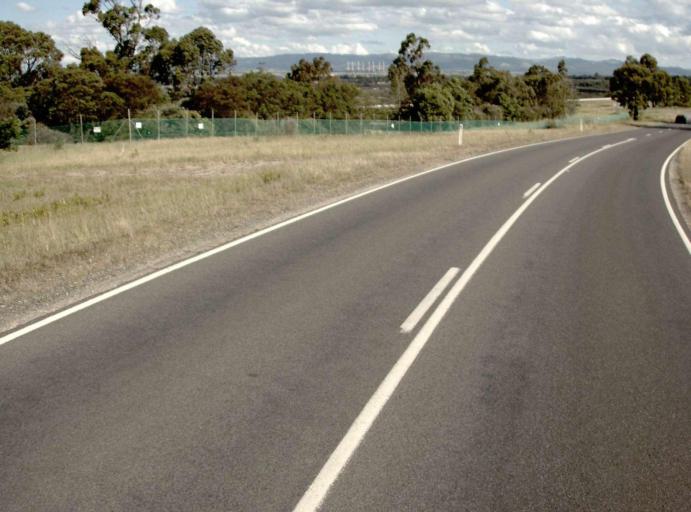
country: AU
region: Victoria
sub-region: Latrobe
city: Moe
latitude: -38.1980
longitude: 146.3274
